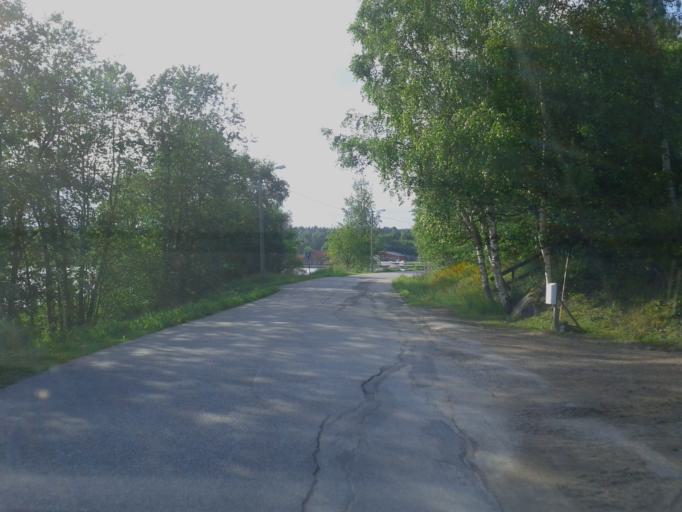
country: SE
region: Vaesternorrland
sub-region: OErnskoeldsviks Kommun
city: Ornskoldsvik
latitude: 63.2661
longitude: 18.8077
